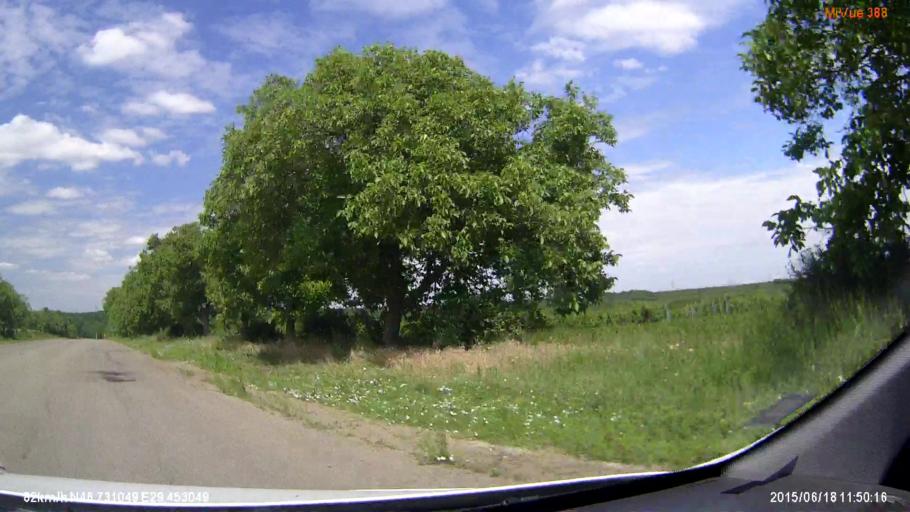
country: MD
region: Causeni
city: Causeni
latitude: 46.7306
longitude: 29.4531
